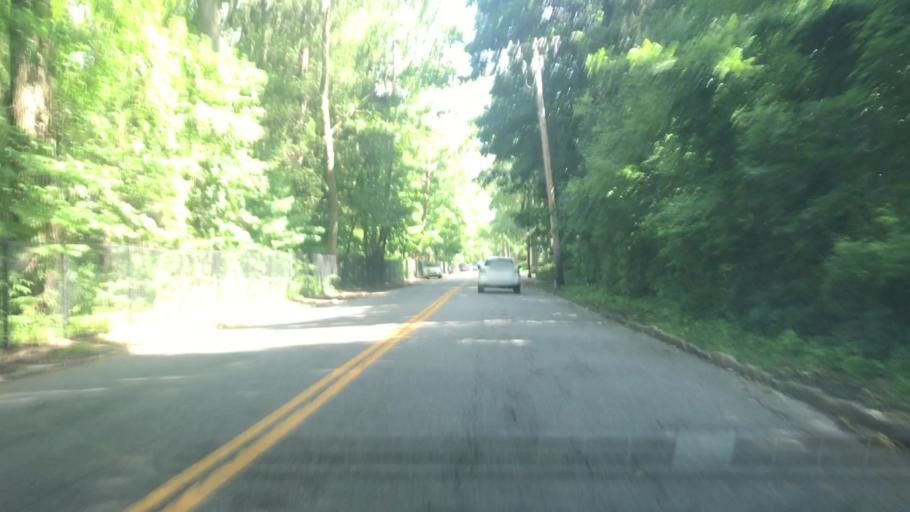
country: US
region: New York
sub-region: Westchester County
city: Tuckahoe
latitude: 40.9623
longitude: -73.8067
